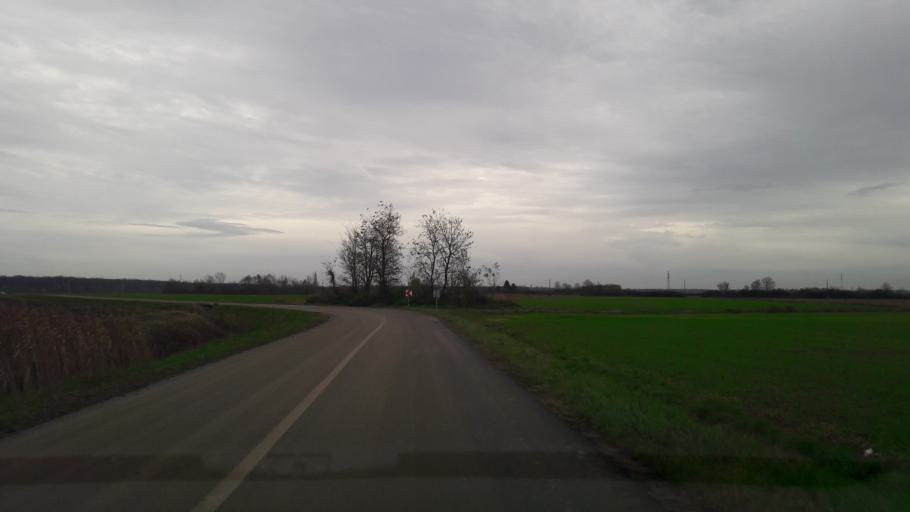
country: HR
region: Virovitick-Podravska
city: Zdenci
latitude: 45.6086
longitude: 18.0502
